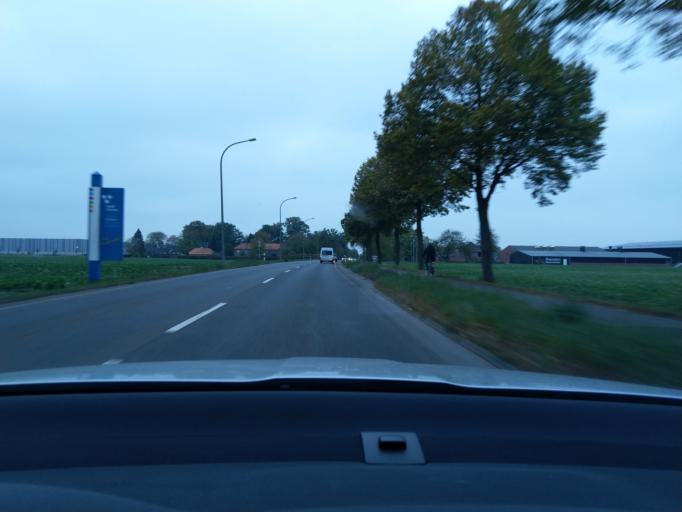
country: DE
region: North Rhine-Westphalia
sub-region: Regierungsbezirk Dusseldorf
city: Schwalmtal
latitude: 51.2425
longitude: 6.3277
